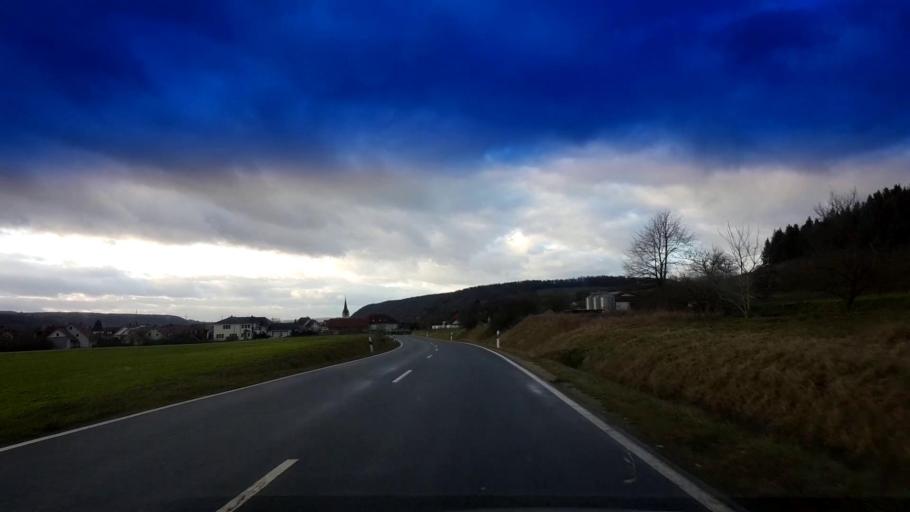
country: DE
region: Bavaria
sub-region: Regierungsbezirk Unterfranken
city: Stettfeld
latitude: 49.9683
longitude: 10.7341
